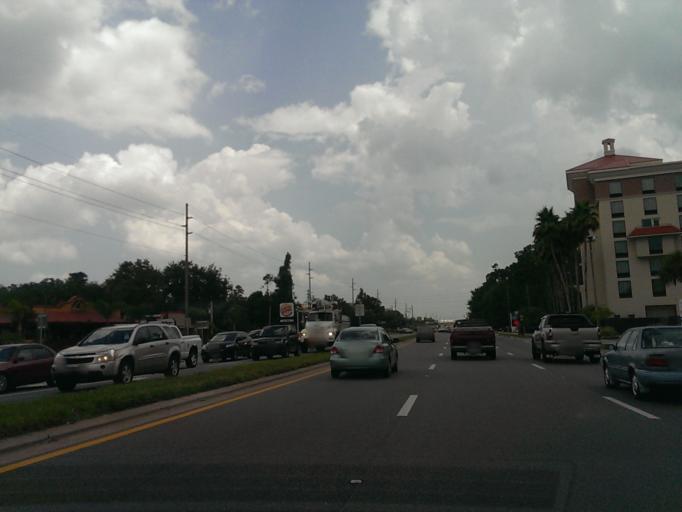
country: US
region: Florida
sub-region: Orange County
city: Doctor Phillips
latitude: 28.3853
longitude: -81.5062
